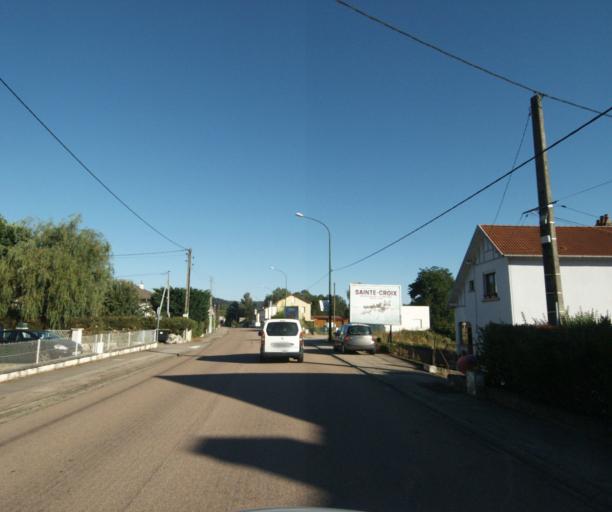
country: FR
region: Lorraine
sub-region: Departement des Vosges
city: Chantraine
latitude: 48.1473
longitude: 6.4620
